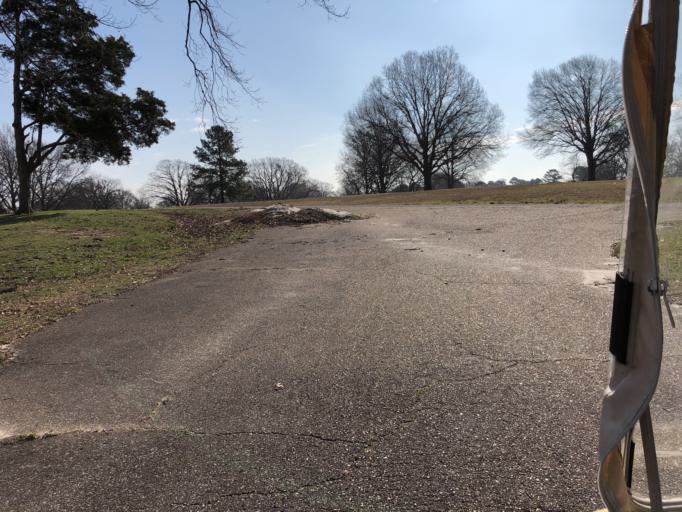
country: US
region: Tennessee
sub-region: Shelby County
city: New South Memphis
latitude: 35.0835
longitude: -89.9927
